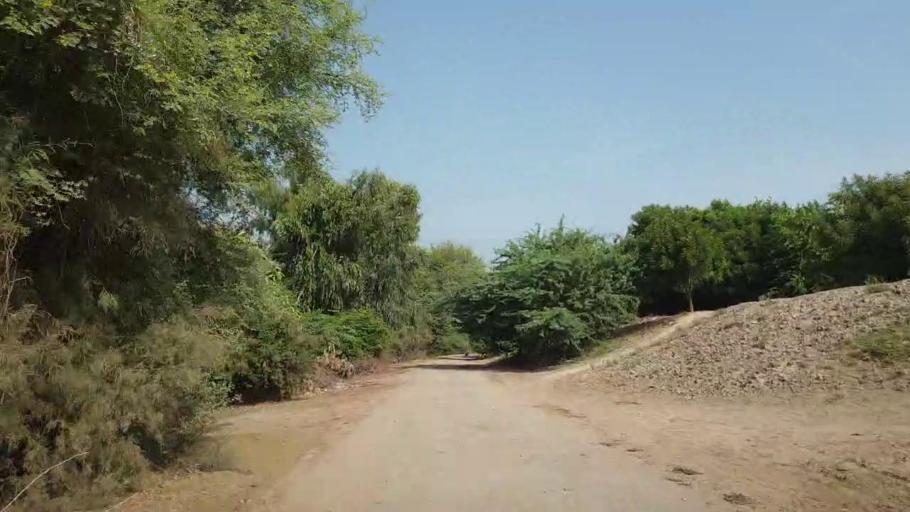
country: PK
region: Sindh
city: Larkana
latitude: 27.4799
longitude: 68.2563
